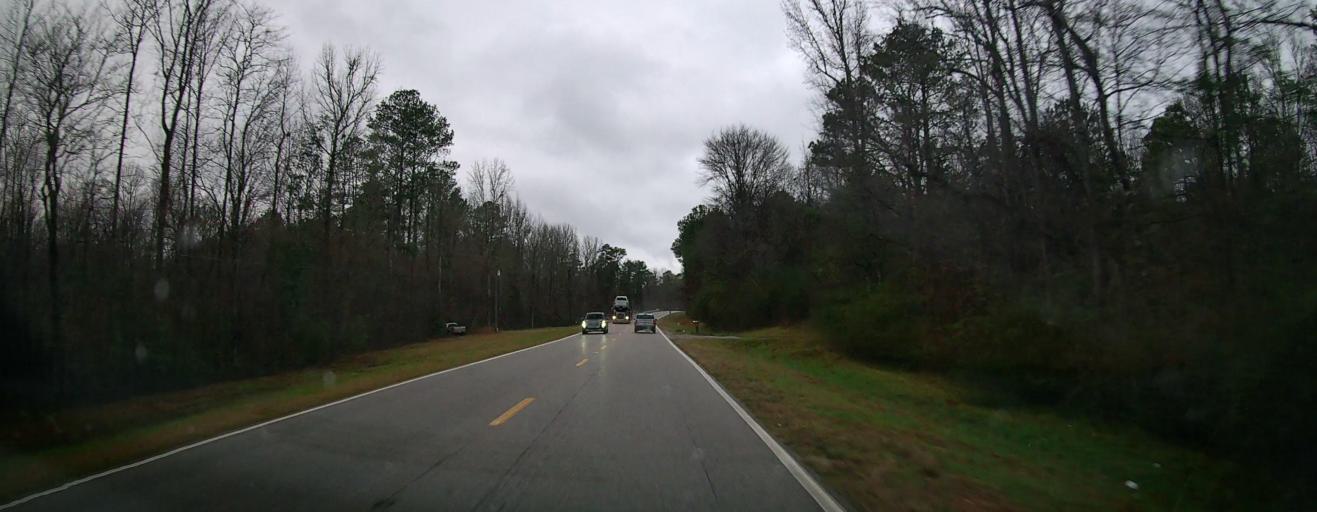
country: US
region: Alabama
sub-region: Bibb County
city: Centreville
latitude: 32.9095
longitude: -87.0207
